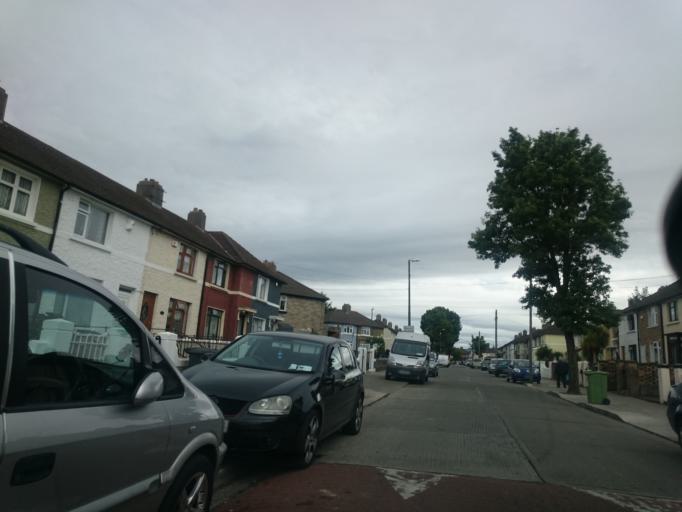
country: IE
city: Greenhills
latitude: 53.3268
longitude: -6.3059
